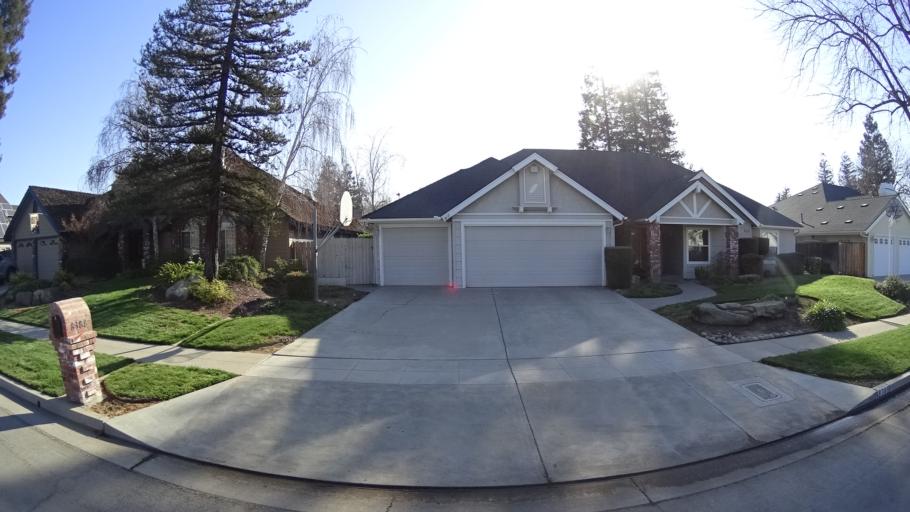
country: US
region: California
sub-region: Fresno County
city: Clovis
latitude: 36.8579
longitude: -119.7945
